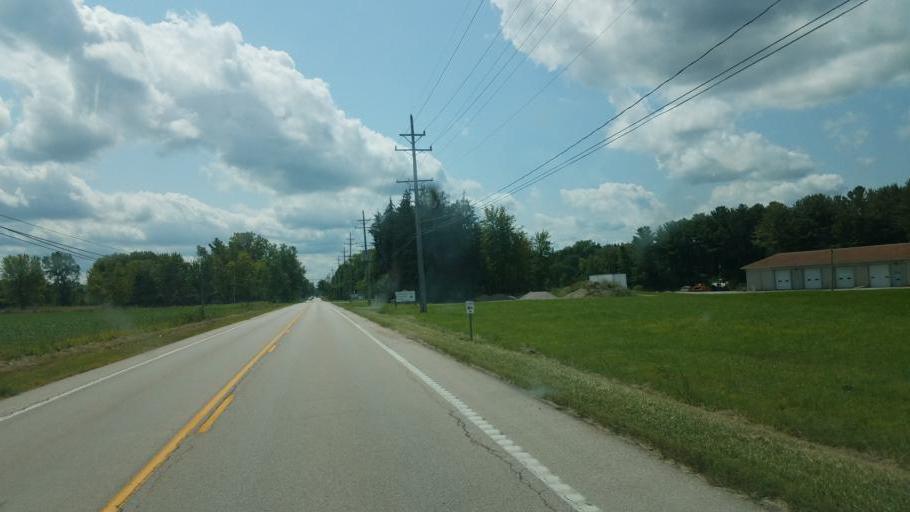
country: US
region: Ohio
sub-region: Ashtabula County
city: Roaming Shores
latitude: 41.6747
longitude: -80.8561
